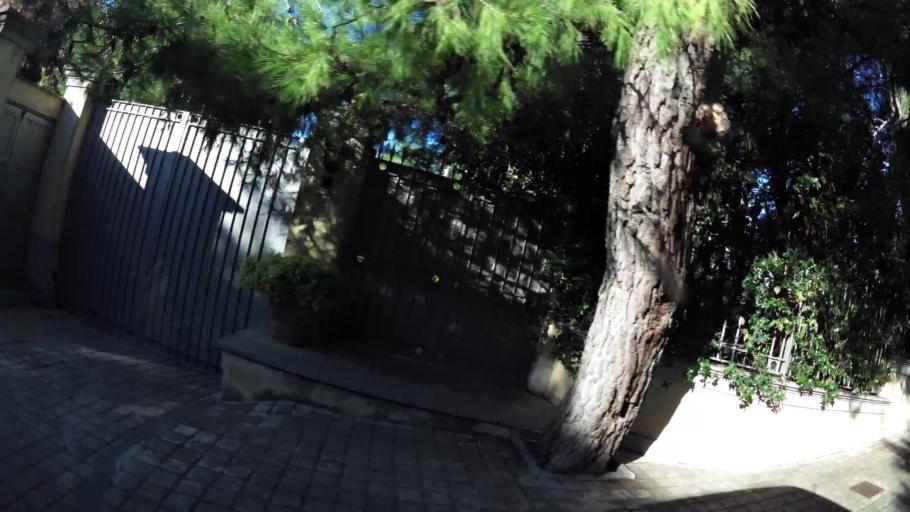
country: GR
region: Attica
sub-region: Nomarchia Athinas
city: Ekali
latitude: 38.1070
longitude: 23.8434
